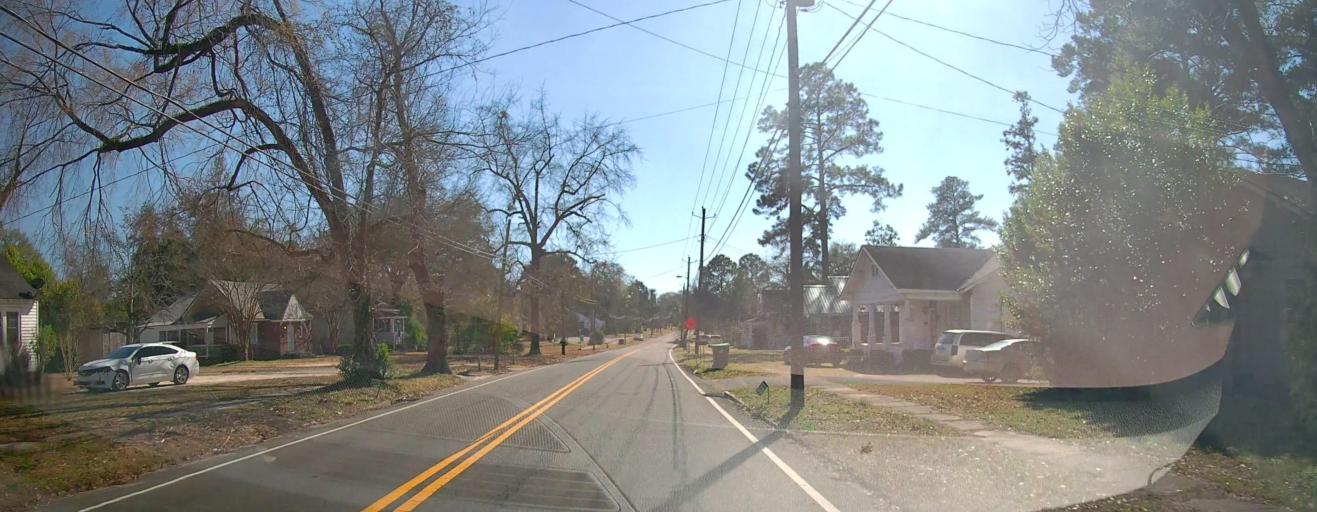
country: US
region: Georgia
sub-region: Macon County
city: Montezuma
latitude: 32.3106
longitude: -84.0252
